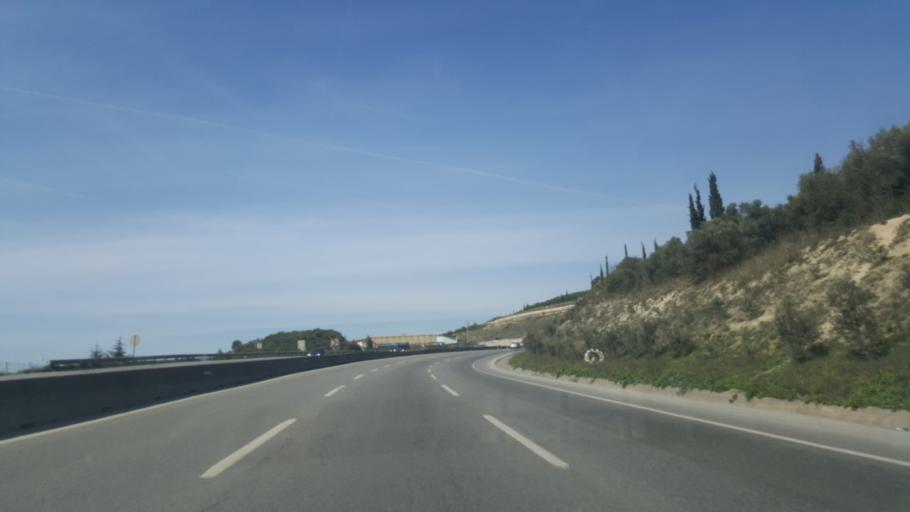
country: TR
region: Kocaeli
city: Tavsancil
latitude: 40.7737
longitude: 29.5578
